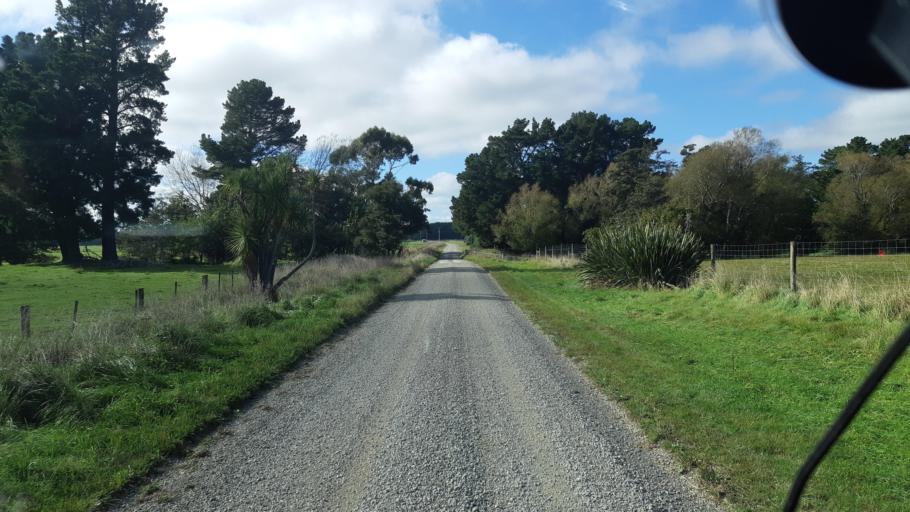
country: NZ
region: Canterbury
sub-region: Waimakariri District
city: Oxford
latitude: -43.2138
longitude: 172.4147
